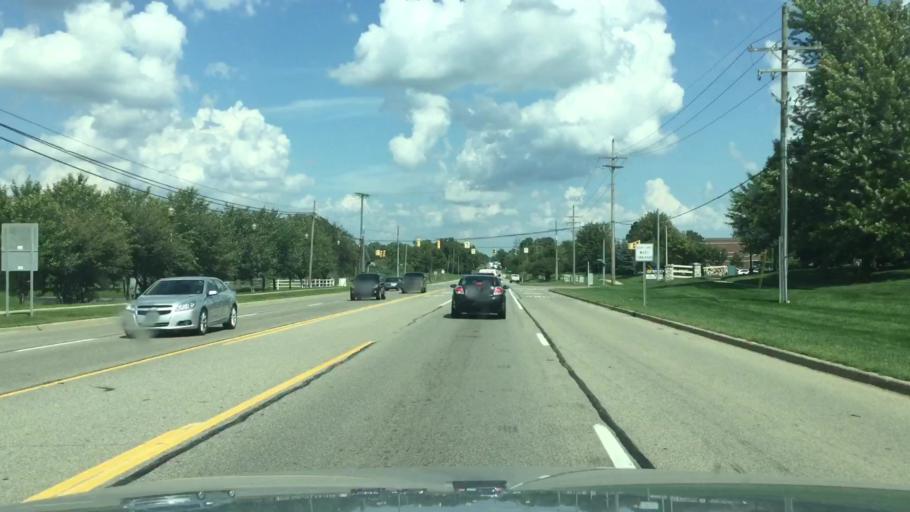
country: US
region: Michigan
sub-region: Washtenaw County
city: Saline
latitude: 42.1764
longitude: -83.7588
